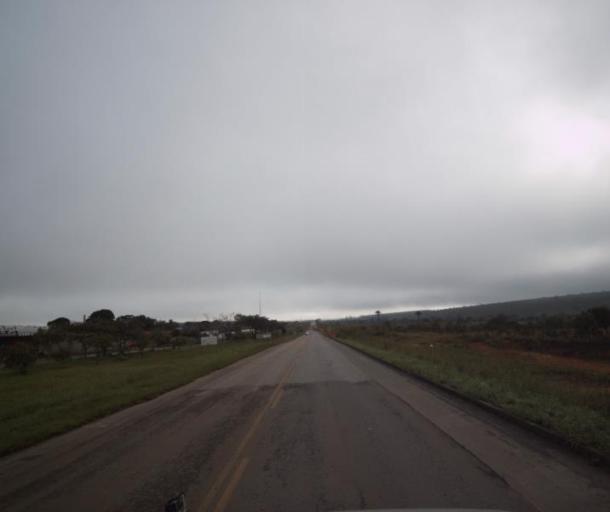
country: BR
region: Goias
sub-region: Pirenopolis
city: Pirenopolis
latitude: -15.7745
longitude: -48.7637
